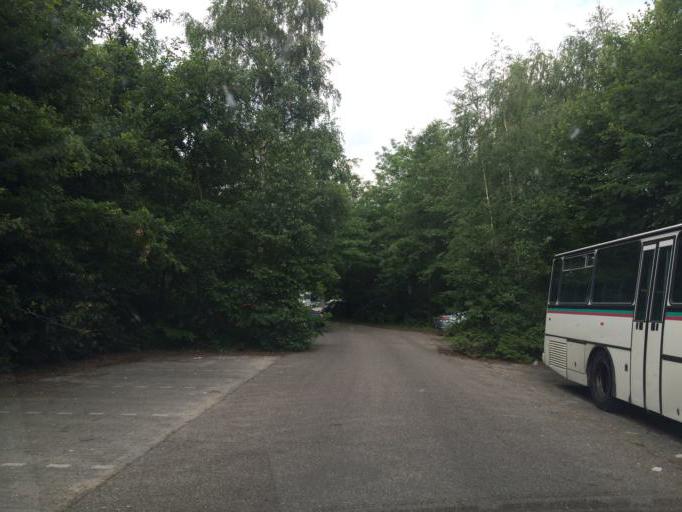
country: BE
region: Flanders
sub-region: Provincie Antwerpen
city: Balen
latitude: 51.2164
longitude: 5.1944
